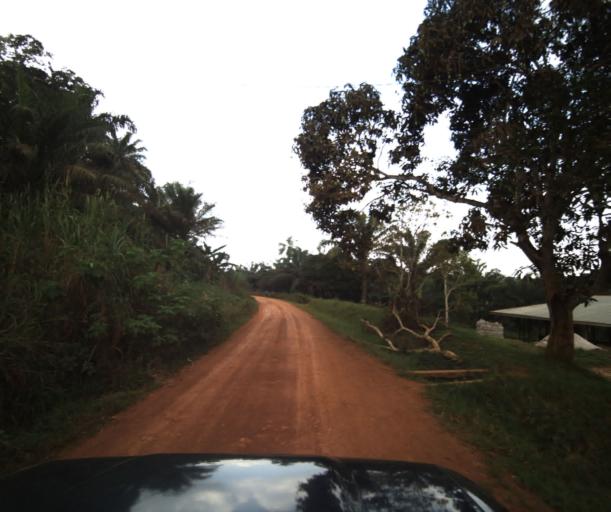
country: CM
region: Centre
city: Akono
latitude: 3.6036
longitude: 11.1889
